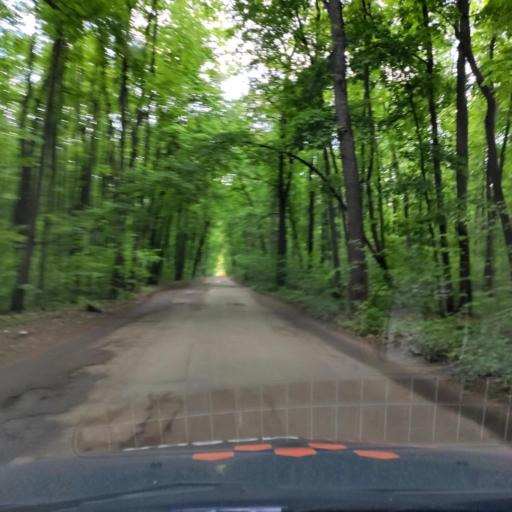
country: RU
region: Voronezj
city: Podgornoye
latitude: 51.7437
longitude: 39.2145
